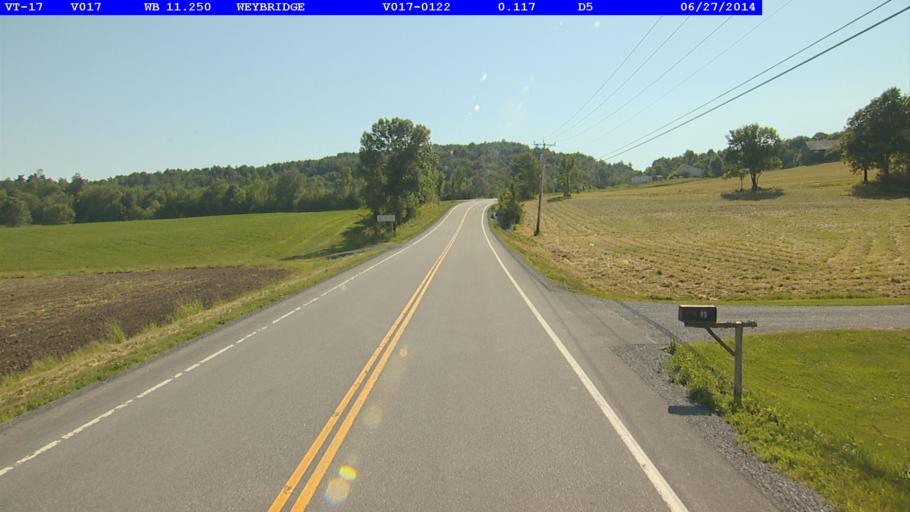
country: US
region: Vermont
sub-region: Addison County
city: Vergennes
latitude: 44.0852
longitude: -73.2483
